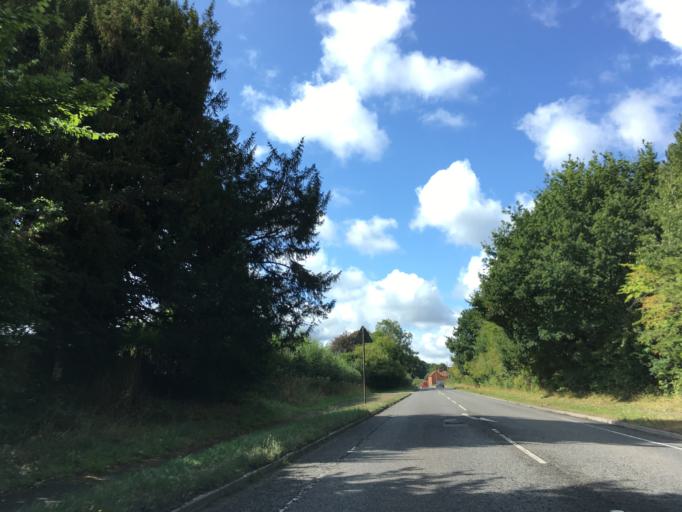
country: GB
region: England
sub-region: West Berkshire
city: Greenham
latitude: 51.3710
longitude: -1.3183
